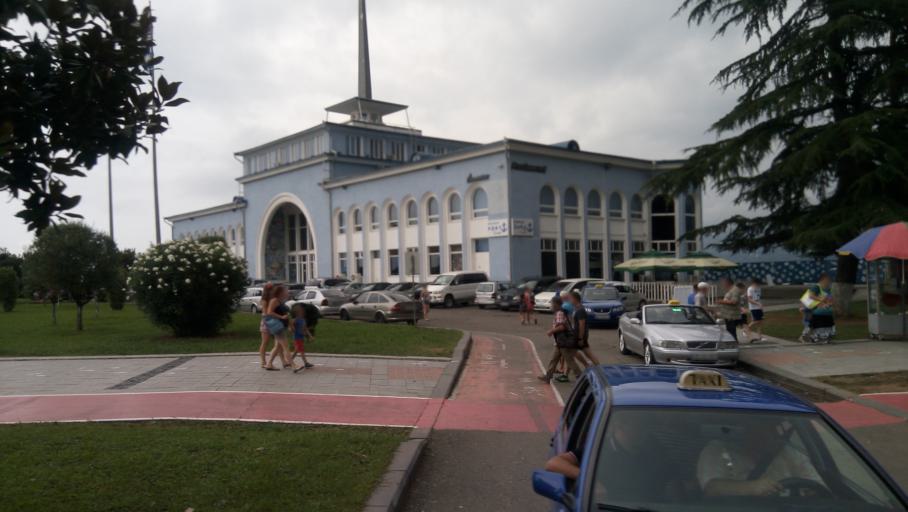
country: GE
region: Ajaria
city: Batumi
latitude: 41.6515
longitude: 41.6434
